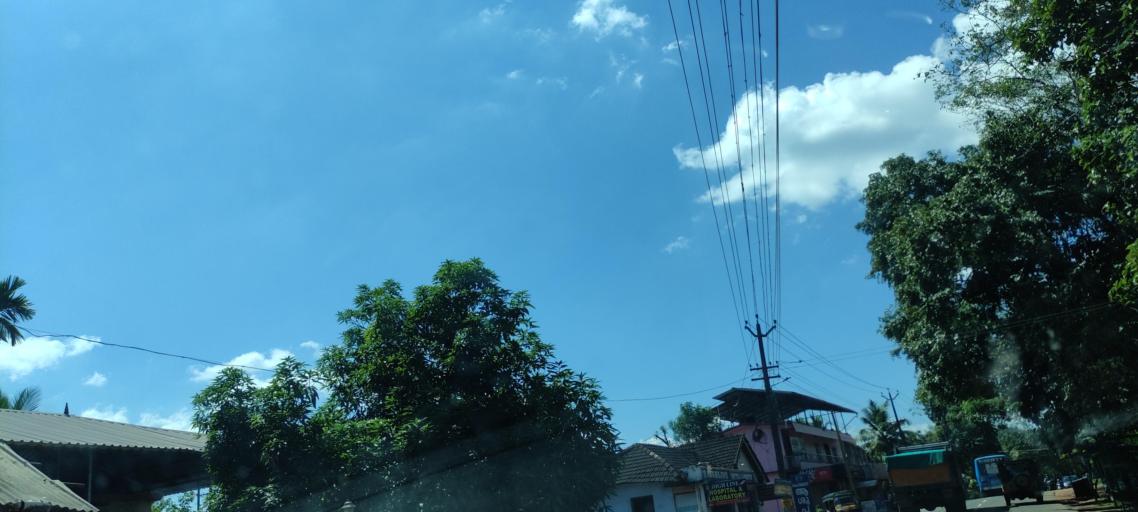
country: IN
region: Kerala
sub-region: Pattanamtitta
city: Adur
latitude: 9.1068
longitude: 76.6942
